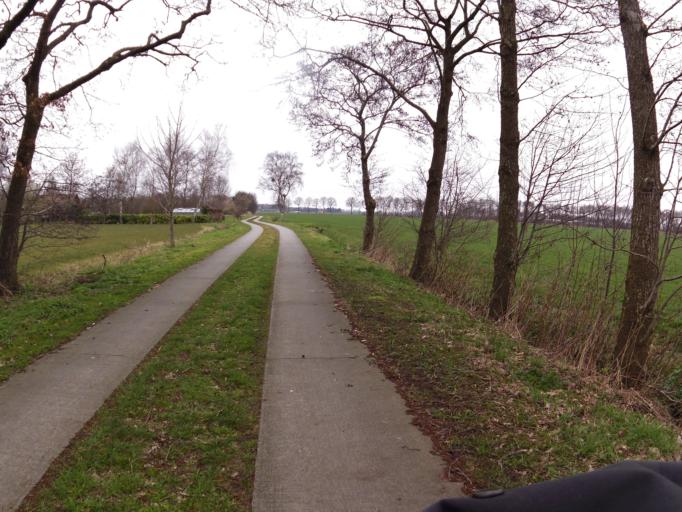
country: NL
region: Drenthe
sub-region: Gemeente Westerveld
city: Dwingeloo
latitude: 52.9640
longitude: 6.3567
